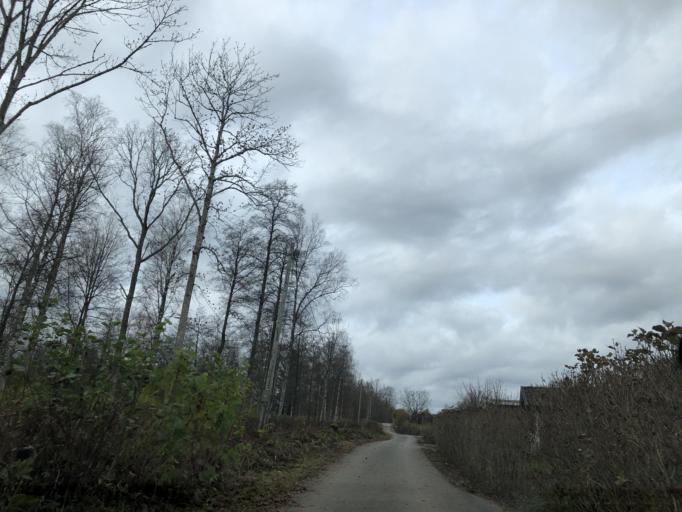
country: SE
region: Vaestra Goetaland
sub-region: Ulricehamns Kommun
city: Ulricehamn
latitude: 57.7149
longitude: 13.3678
